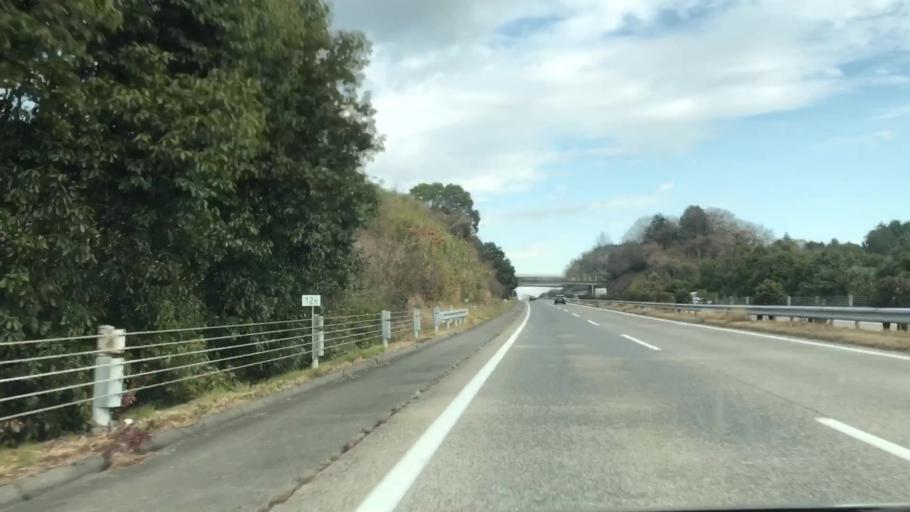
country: JP
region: Saga Prefecture
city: Kanzakimachi-kanzaki
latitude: 33.3556
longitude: 130.4190
